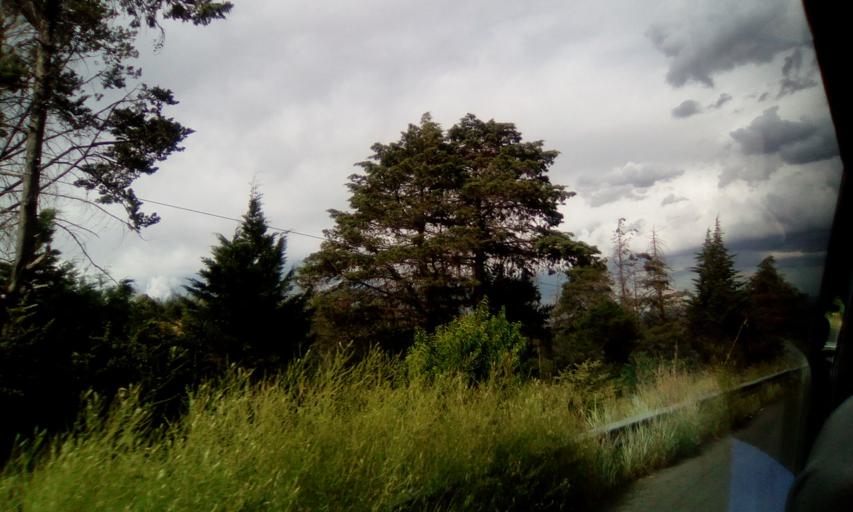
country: ZA
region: Orange Free State
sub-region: Thabo Mofutsanyana District Municipality
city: Ladybrand
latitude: -29.2128
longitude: 27.4553
